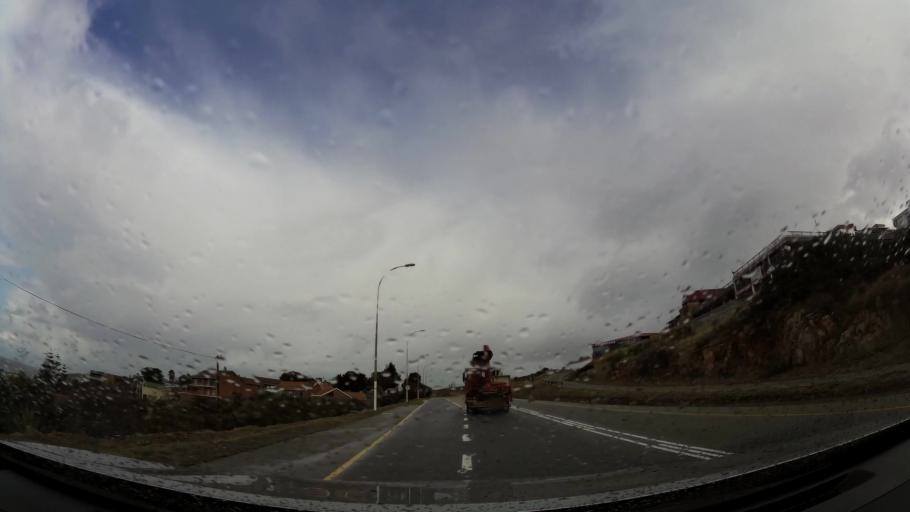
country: ZA
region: Western Cape
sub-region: Eden District Municipality
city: Mossel Bay
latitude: -34.1800
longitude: 22.1335
